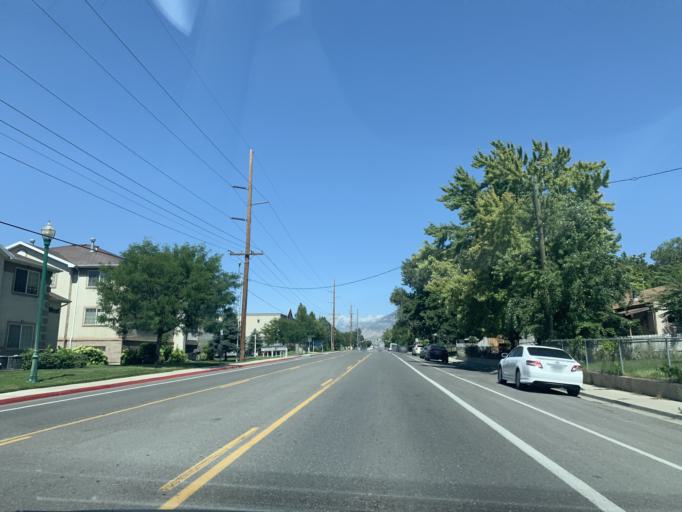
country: US
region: Utah
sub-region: Utah County
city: Orem
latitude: 40.2867
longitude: -111.7241
